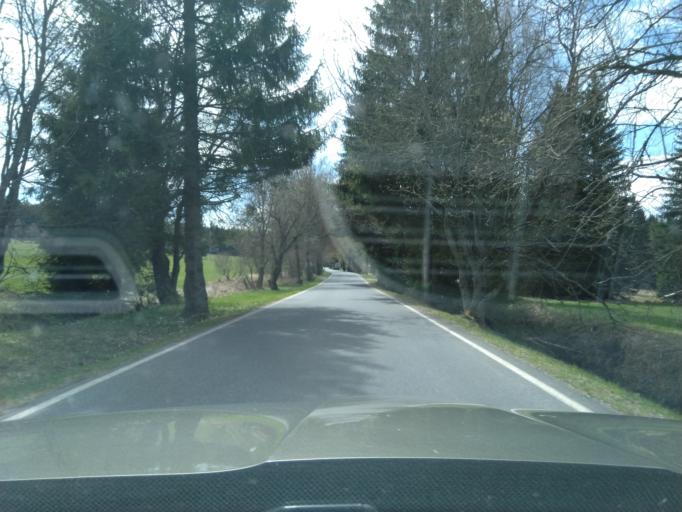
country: CZ
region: Jihocesky
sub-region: Okres Prachatice
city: Borova Lada
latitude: 49.0231
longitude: 13.6665
